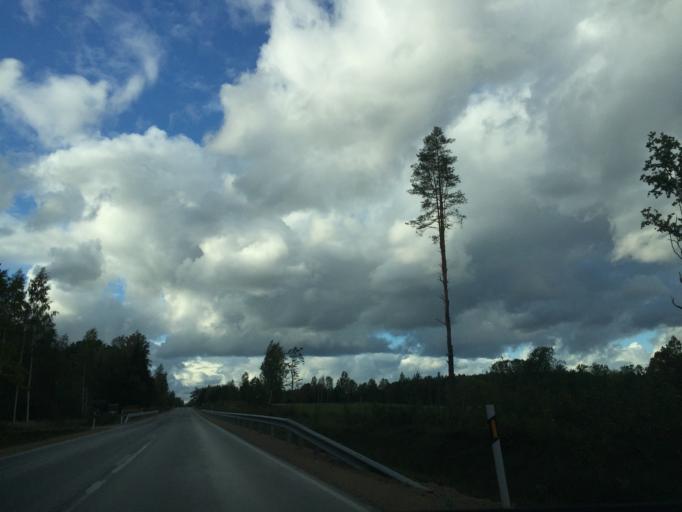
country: LV
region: Ligatne
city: Ligatne
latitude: 57.1686
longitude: 25.0461
